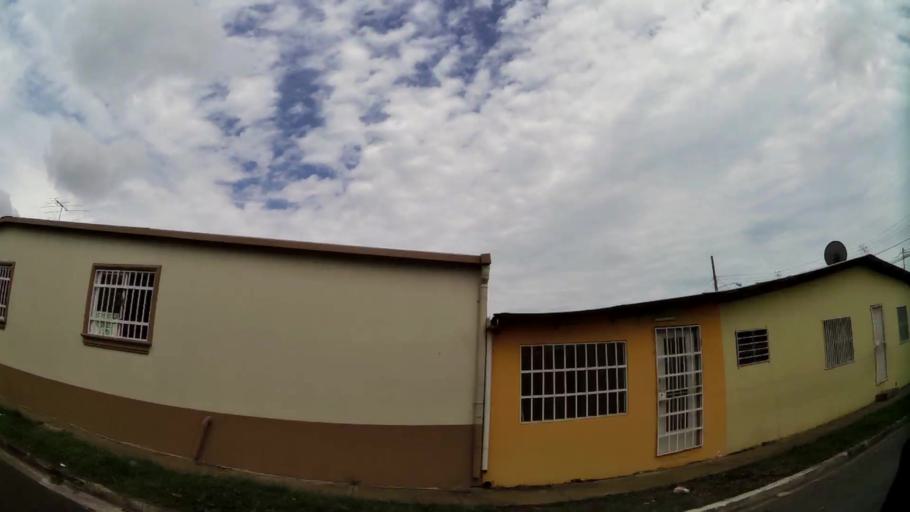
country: PA
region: Panama
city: Tocumen
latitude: 9.0522
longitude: -79.4177
